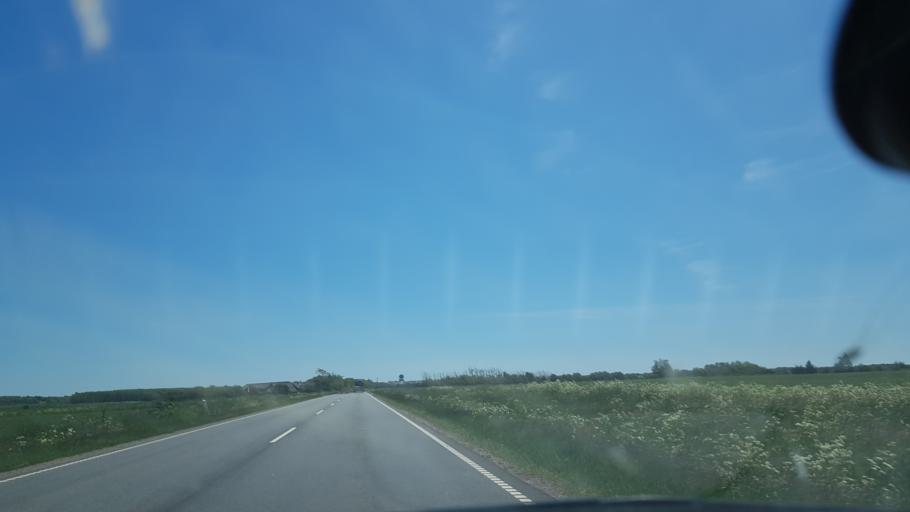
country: DK
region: South Denmark
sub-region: Tonder Kommune
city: Sherrebek
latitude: 55.1430
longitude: 8.7896
